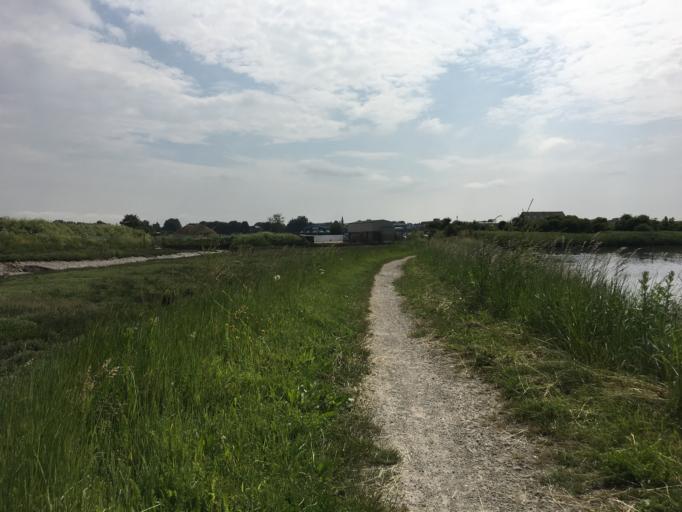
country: GB
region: England
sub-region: Kent
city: Sittingbourne
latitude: 51.3470
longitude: 0.7433
